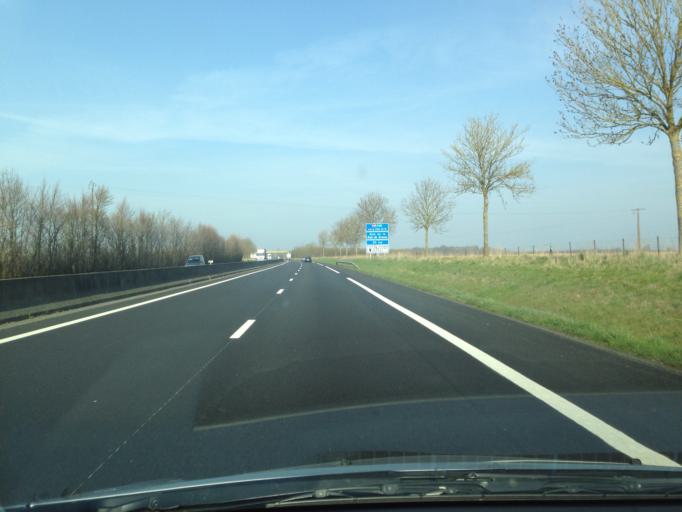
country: FR
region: Picardie
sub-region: Departement de la Somme
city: Oisemont
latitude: 50.0295
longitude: 1.7410
